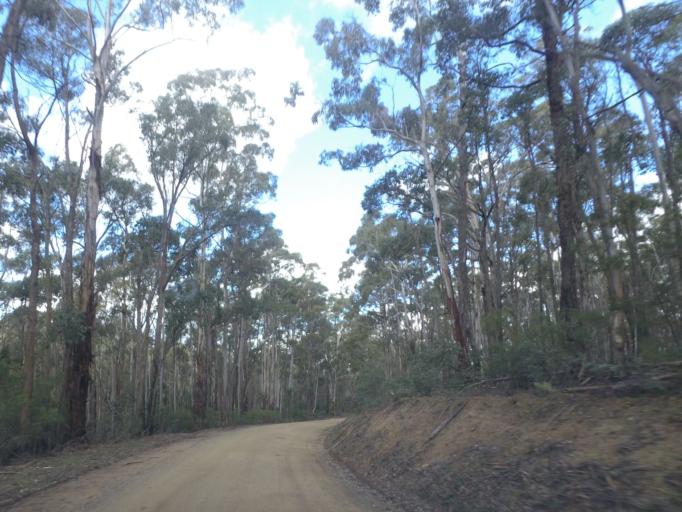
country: AU
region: Victoria
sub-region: Moorabool
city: Bacchus Marsh
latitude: -37.4661
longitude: 144.4819
